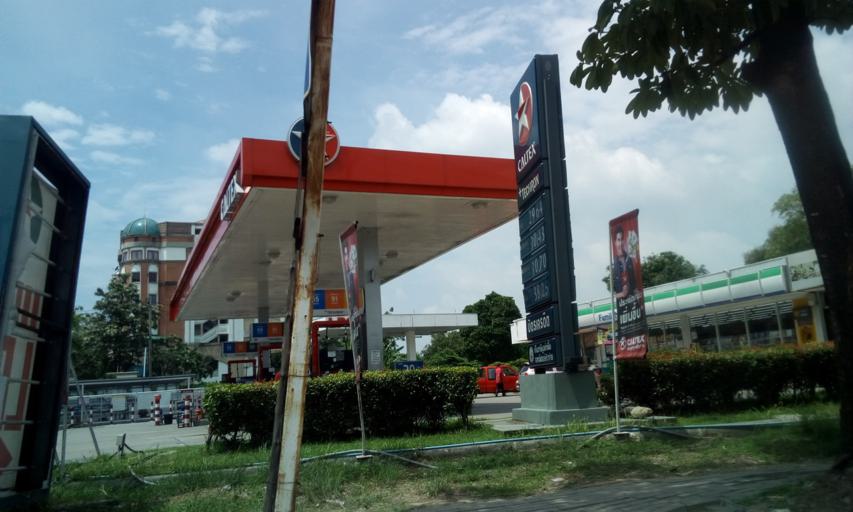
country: TH
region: Bangkok
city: Don Mueang
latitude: 13.9383
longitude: 100.5493
